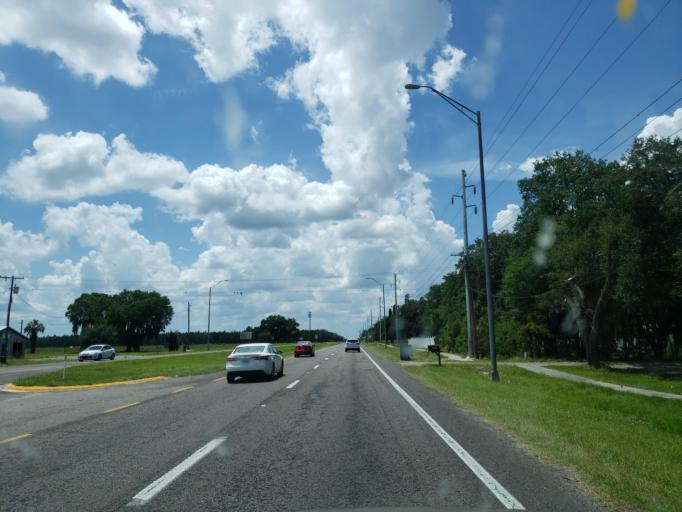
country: US
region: Florida
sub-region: Hillsborough County
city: Plant City
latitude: 27.9378
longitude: -82.1237
